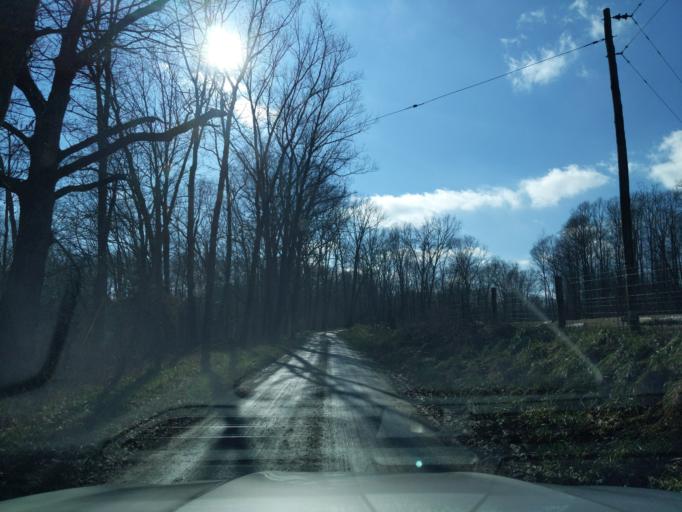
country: US
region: Indiana
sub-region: Decatur County
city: Greensburg
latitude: 39.2427
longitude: -85.4732
